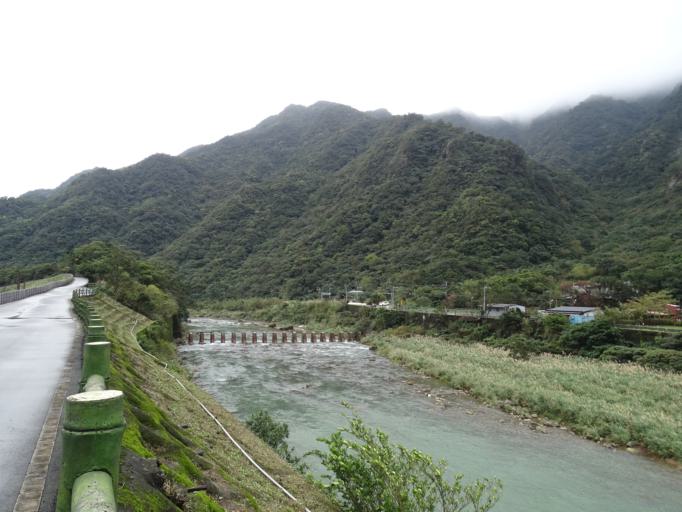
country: TW
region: Taiwan
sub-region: Keelung
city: Keelung
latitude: 25.0965
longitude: 121.8325
